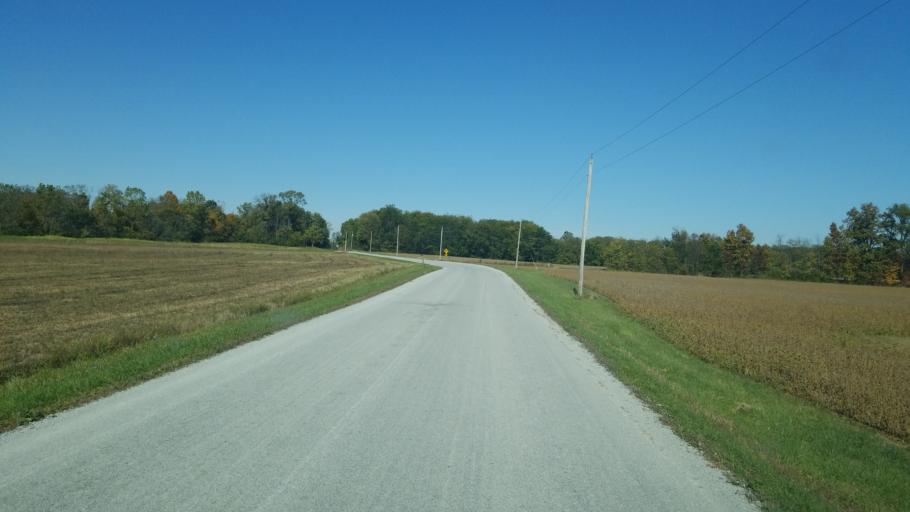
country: US
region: Ohio
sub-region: Hardin County
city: Kenton
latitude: 40.5775
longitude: -83.5048
